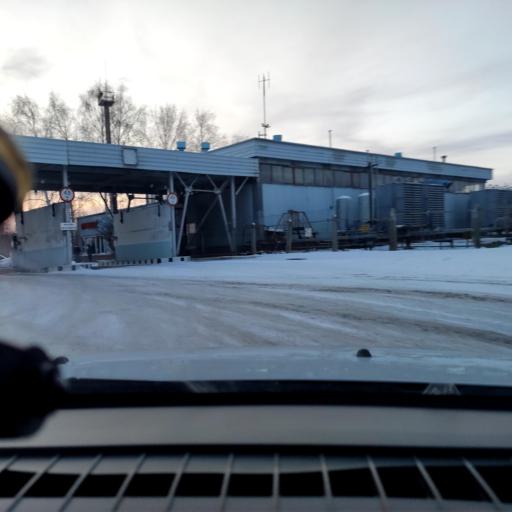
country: RU
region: Samara
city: Chapayevsk
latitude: 53.0055
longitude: 49.7417
